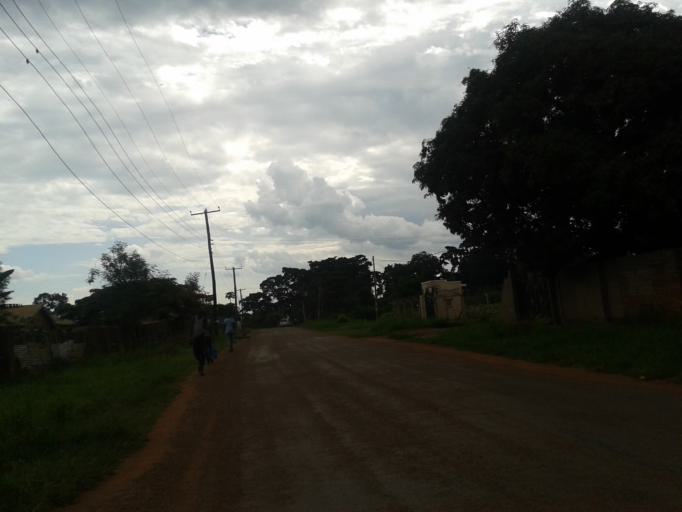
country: UG
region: Northern Region
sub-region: Gulu District
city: Gulu
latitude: 2.7794
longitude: 32.2994
